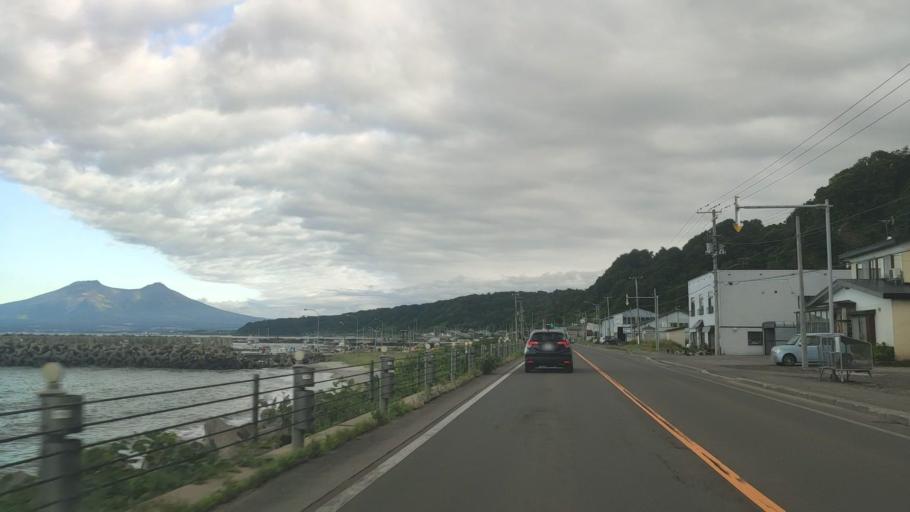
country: JP
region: Hokkaido
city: Nanae
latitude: 42.1366
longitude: 140.5066
